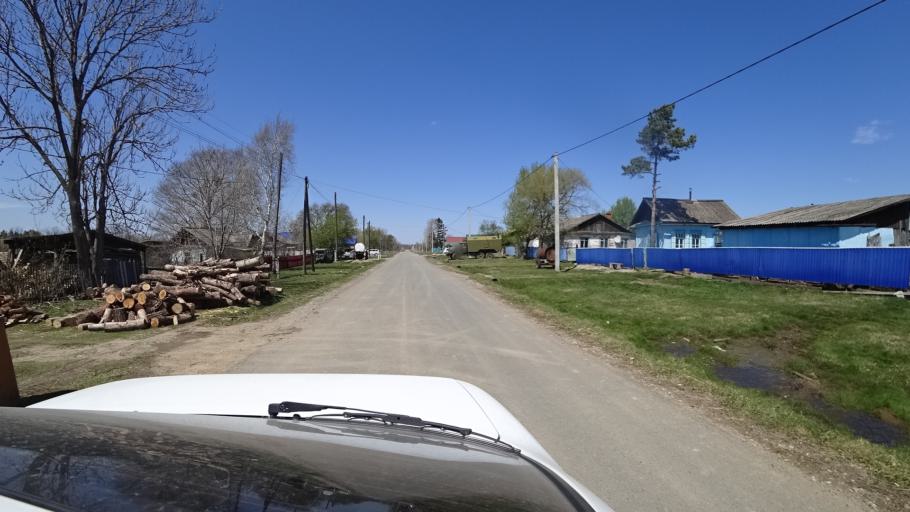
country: RU
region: Primorskiy
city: Dal'nerechensk
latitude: 45.7937
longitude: 133.7718
